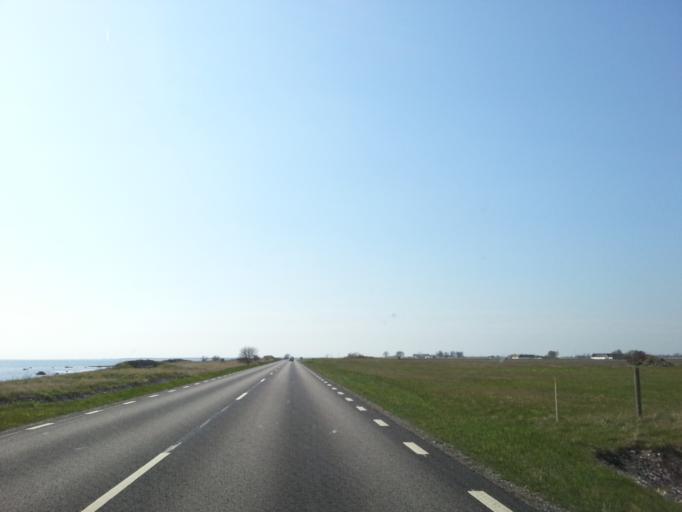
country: SE
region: Skane
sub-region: Trelleborgs Kommun
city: Skare
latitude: 55.3817
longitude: 13.0323
